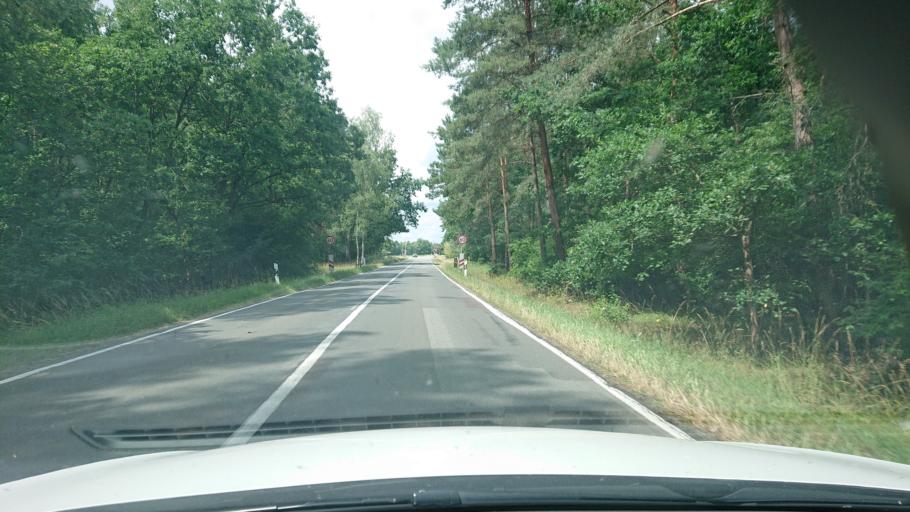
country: DE
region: Mecklenburg-Vorpommern
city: Ludwigslust
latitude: 53.3593
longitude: 11.4737
